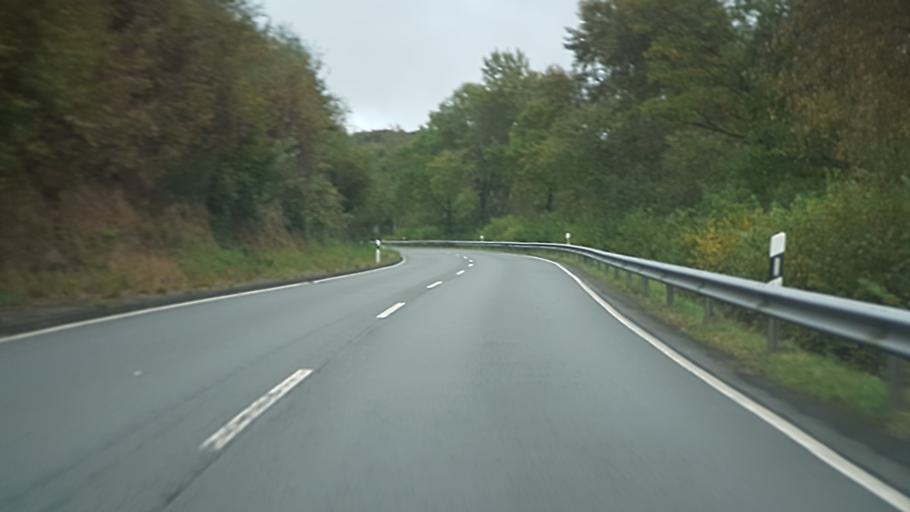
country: DE
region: North Rhine-Westphalia
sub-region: Regierungsbezirk Arnsberg
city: Attendorn
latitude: 51.1488
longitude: 7.8530
